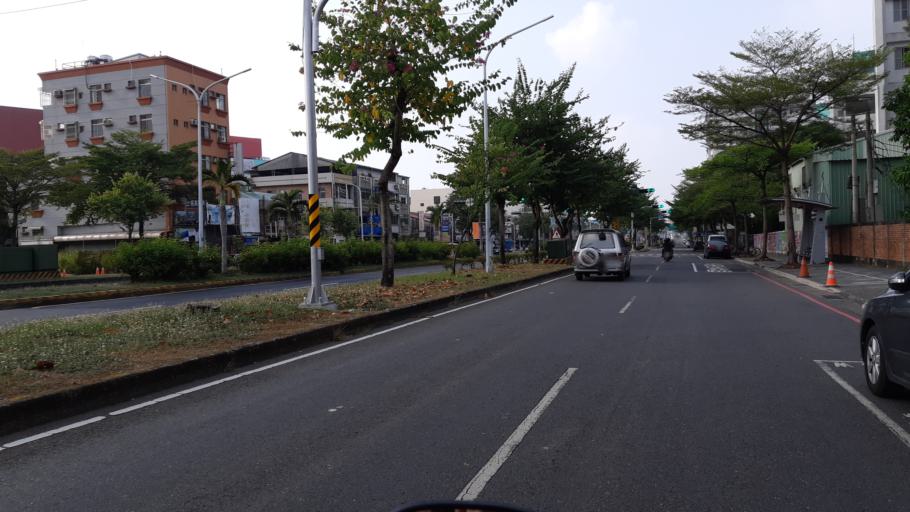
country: TW
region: Taiwan
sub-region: Chiayi
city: Jiayi Shi
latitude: 23.4713
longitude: 120.4647
